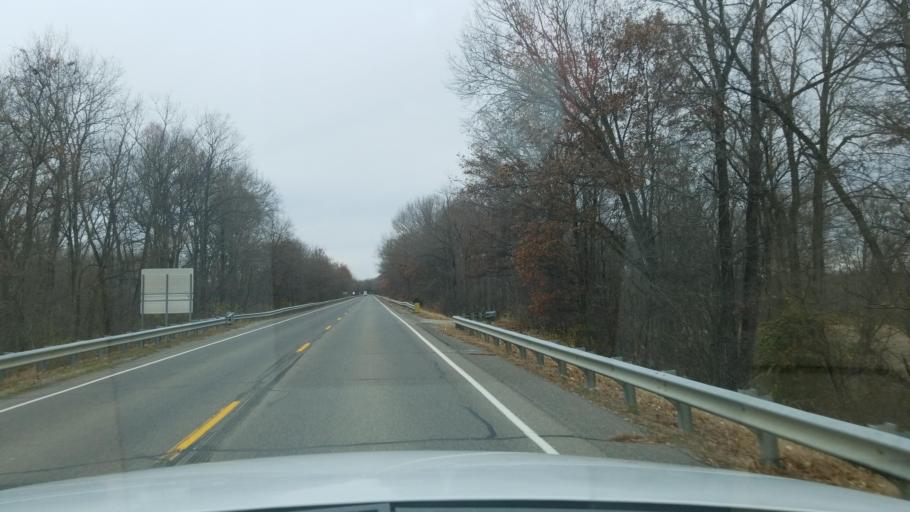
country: US
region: Indiana
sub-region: Posey County
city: Mount Vernon
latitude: 37.9380
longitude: -88.0113
